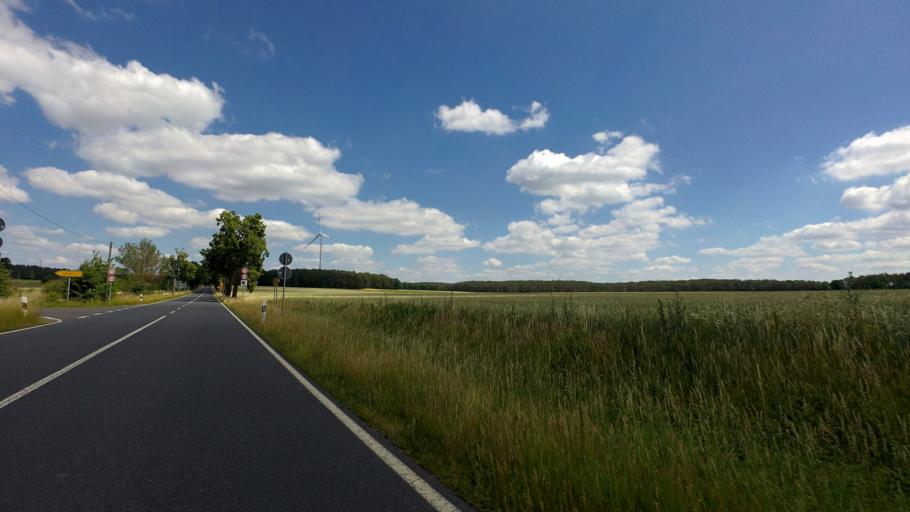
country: DE
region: Brandenburg
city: Sonnewalde
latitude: 51.7135
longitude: 13.6688
